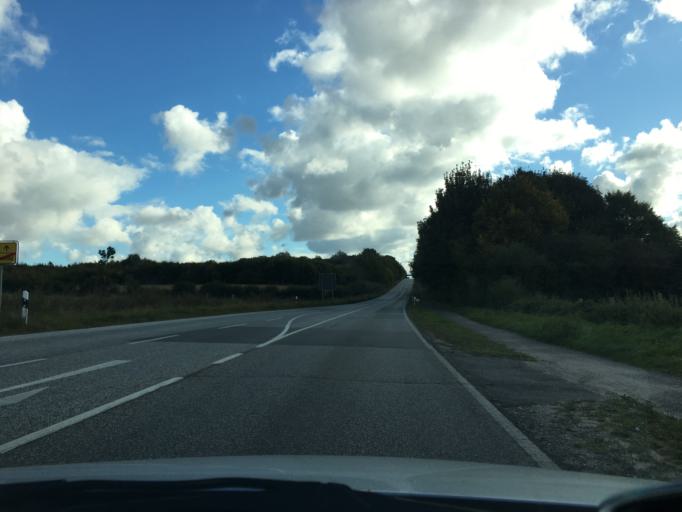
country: DE
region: Schleswig-Holstein
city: Rodenbek
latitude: 54.3038
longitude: 10.0172
